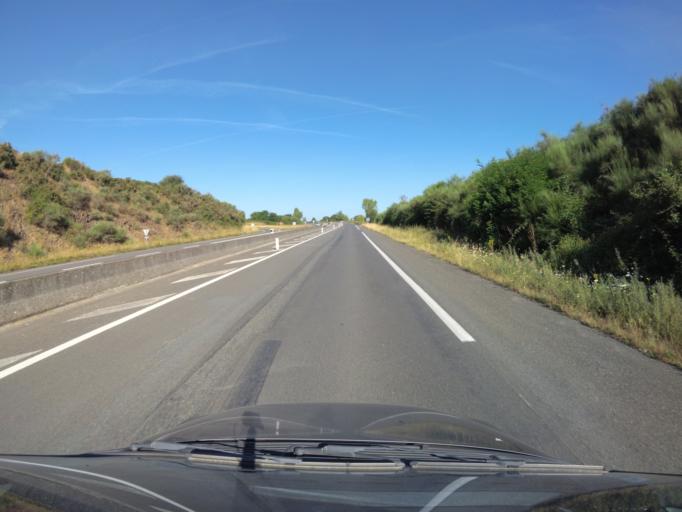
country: FR
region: Pays de la Loire
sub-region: Departement de Maine-et-Loire
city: Vihiers
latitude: 47.1393
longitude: -0.5569
